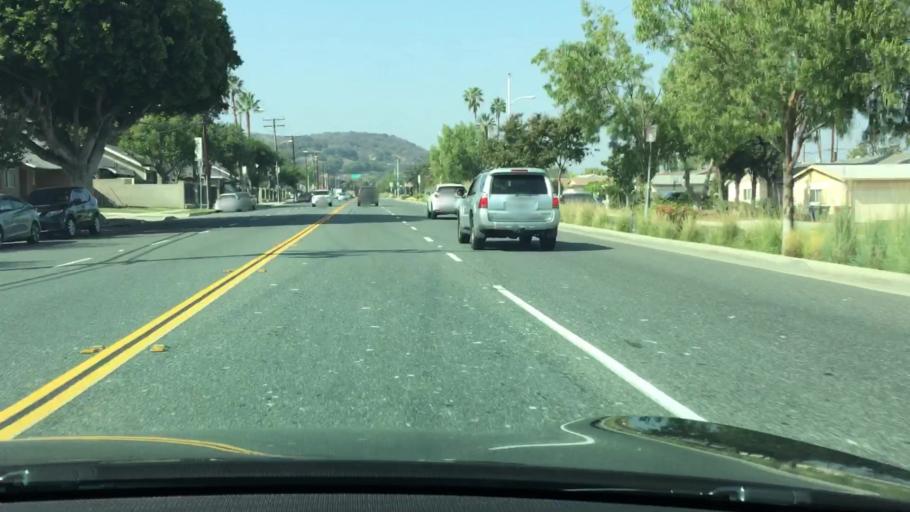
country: US
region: California
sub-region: Los Angeles County
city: Avocado Heights
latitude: 34.0178
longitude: -117.9826
